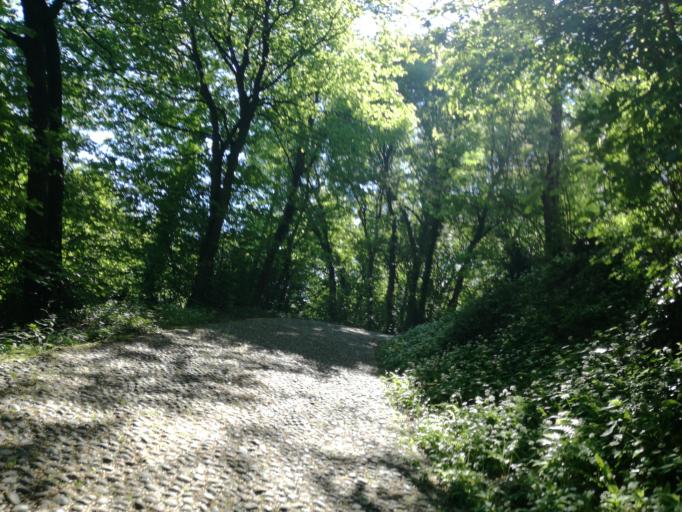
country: IT
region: Lombardy
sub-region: Provincia di Lecco
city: Paderno d'Adda
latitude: 45.6786
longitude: 9.4578
